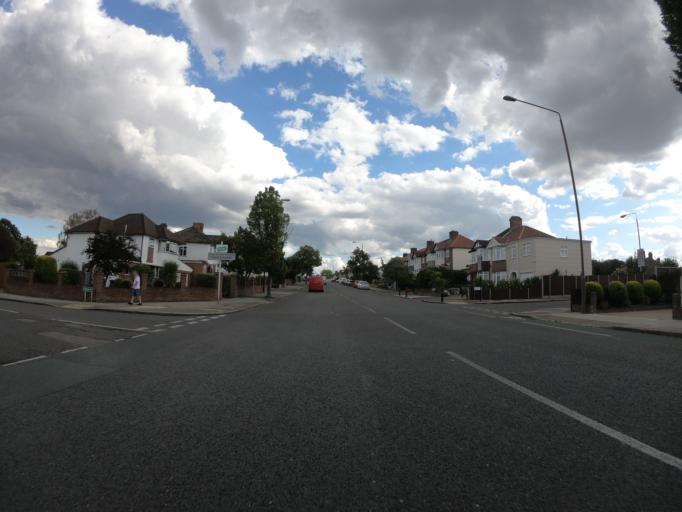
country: GB
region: England
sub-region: Greater London
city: Chislehurst
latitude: 51.4257
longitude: 0.0647
